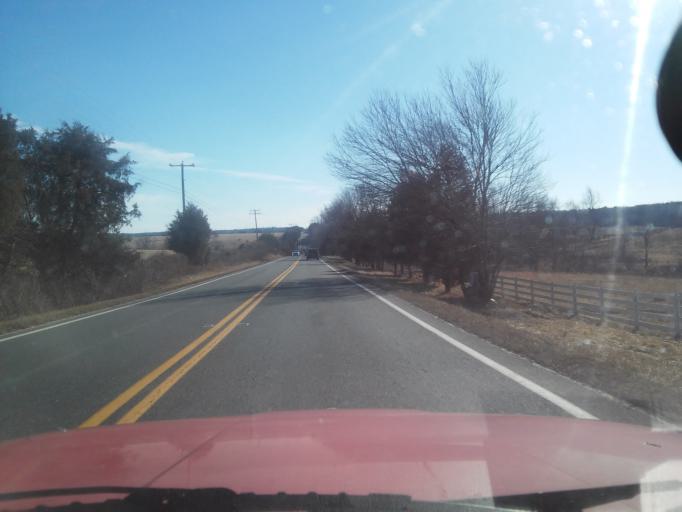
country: US
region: Virginia
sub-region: Orange County
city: Gordonsville
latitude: 38.0353
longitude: -78.1898
